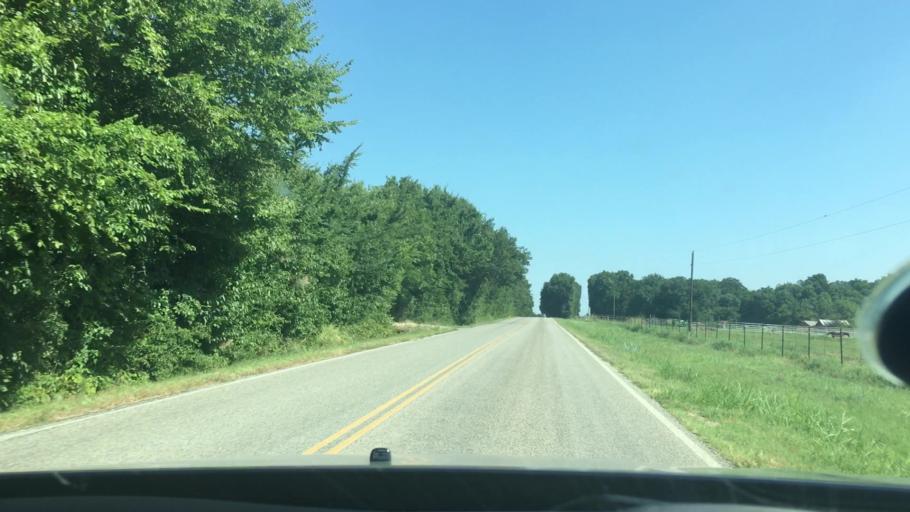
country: US
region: Oklahoma
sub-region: Johnston County
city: Tishomingo
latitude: 34.2932
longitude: -96.6185
